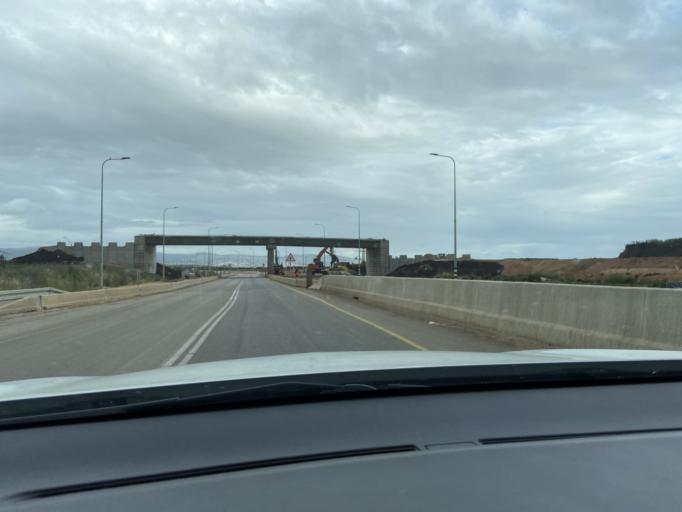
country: IL
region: Northern District
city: El Mazra`a
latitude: 32.9781
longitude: 35.1125
